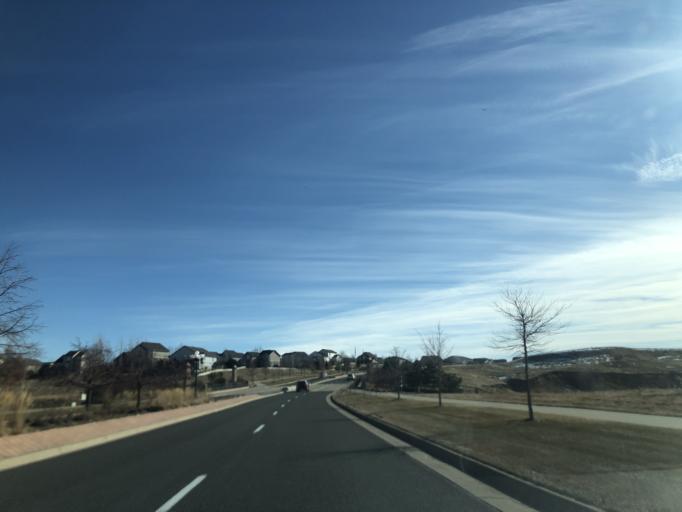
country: US
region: Colorado
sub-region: Arapahoe County
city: Dove Valley
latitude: 39.5614
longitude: -104.8097
